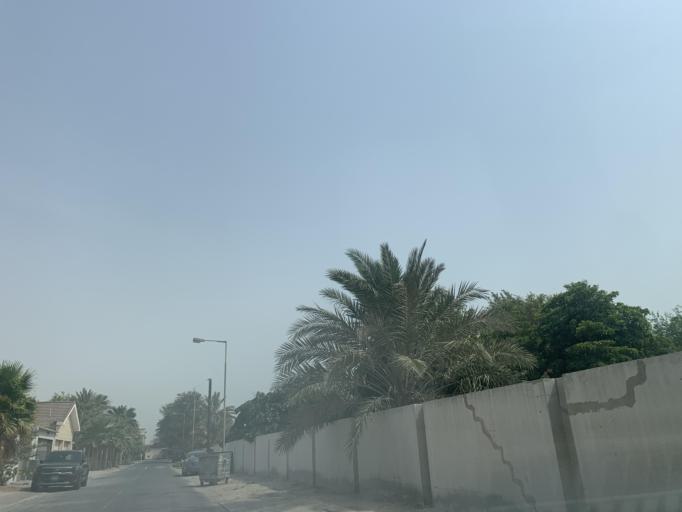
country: BH
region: Manama
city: Jidd Hafs
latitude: 26.2045
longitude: 50.4622
